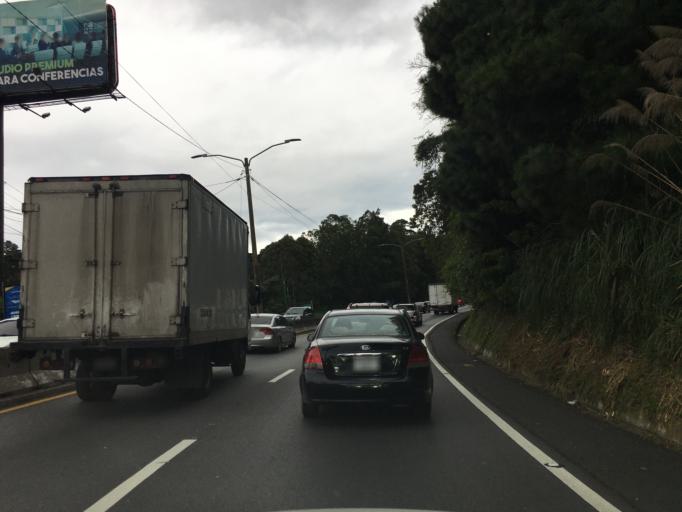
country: GT
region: Guatemala
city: Santa Catarina Pinula
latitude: 14.5791
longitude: -90.4716
